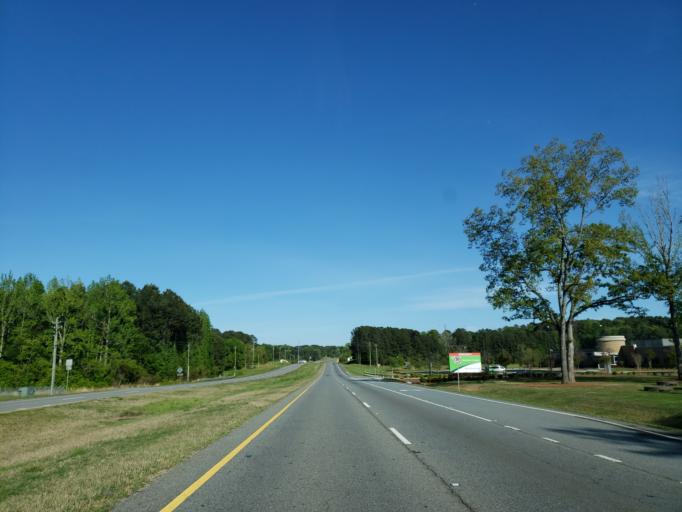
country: US
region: Georgia
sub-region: Polk County
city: Cedartown
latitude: 34.0155
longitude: -85.1972
